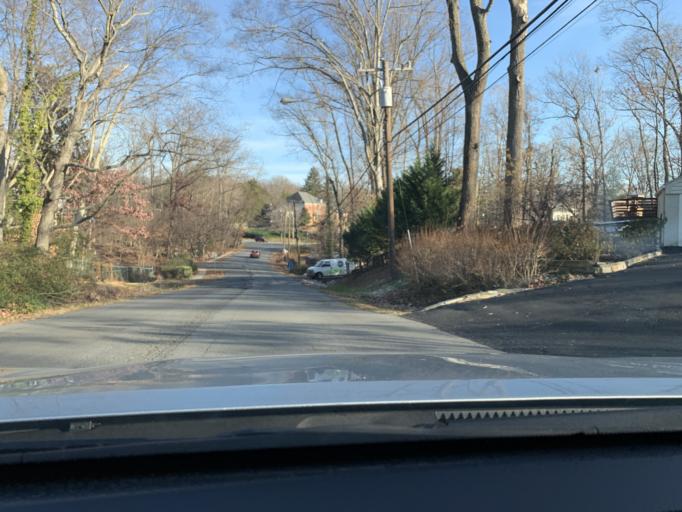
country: US
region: Virginia
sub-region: Fairfax County
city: Jefferson
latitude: 38.8492
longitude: -77.1759
